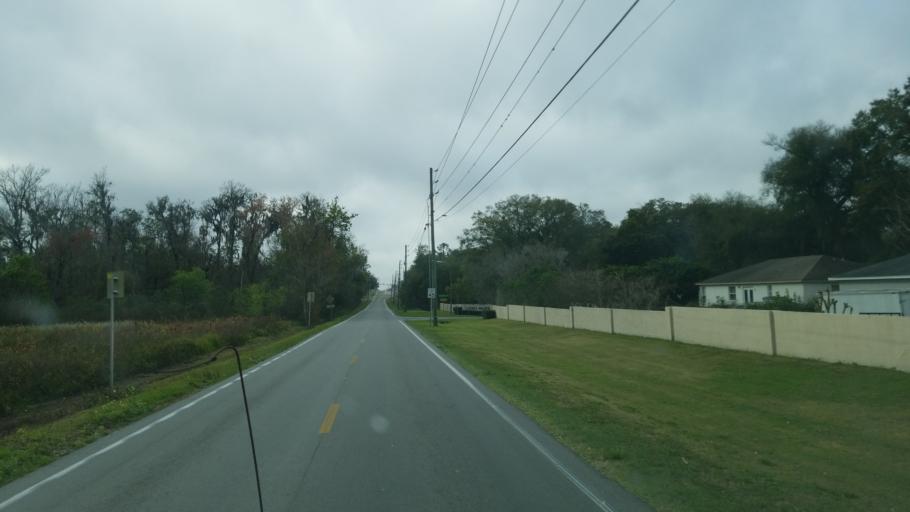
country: US
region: Florida
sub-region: Polk County
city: Kathleen
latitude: 28.1421
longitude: -82.0234
